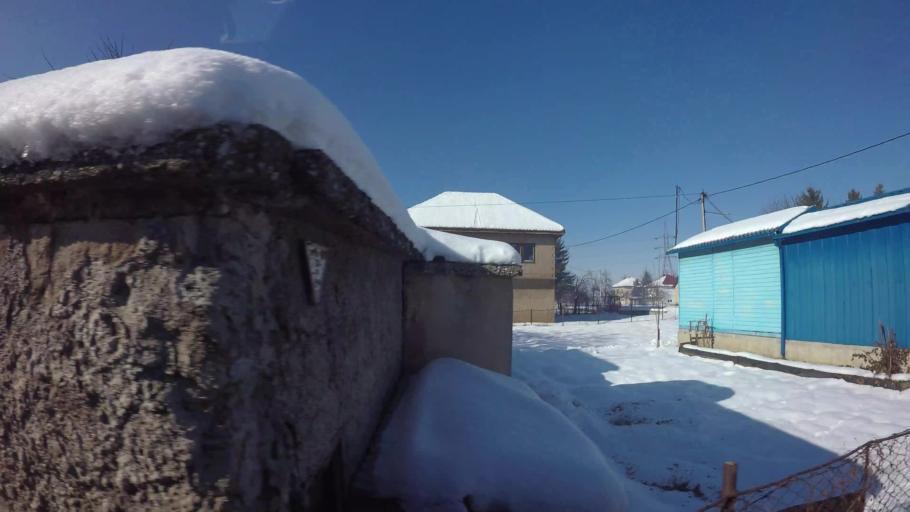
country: BA
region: Federation of Bosnia and Herzegovina
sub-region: Kanton Sarajevo
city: Sarajevo
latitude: 43.7912
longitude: 18.3355
